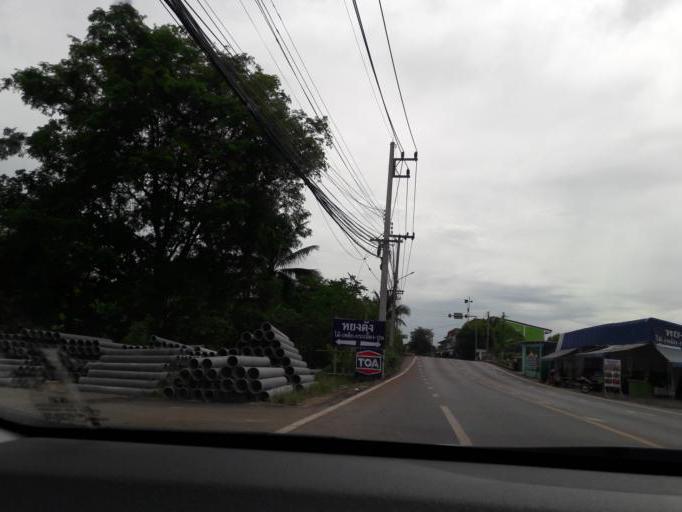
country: TH
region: Ratchaburi
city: Damnoen Saduak
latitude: 13.5514
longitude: 100.0320
